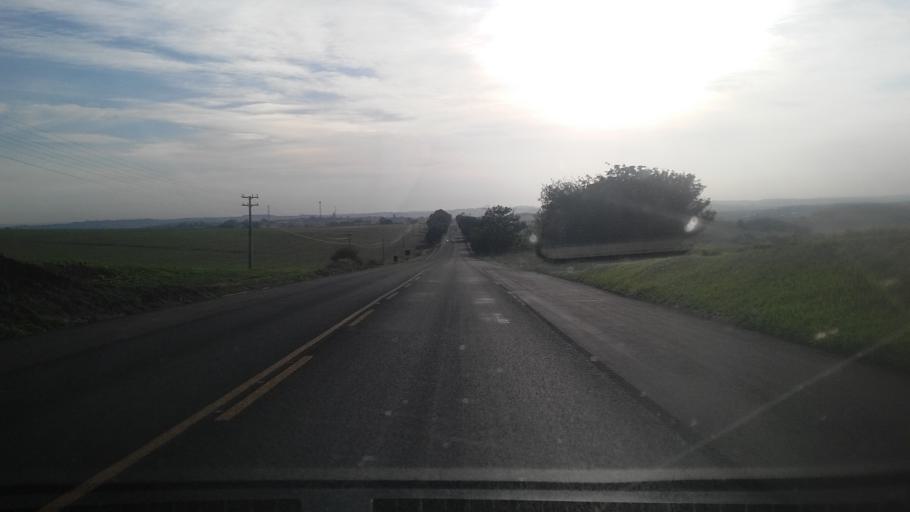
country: BR
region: Parana
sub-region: Bandeirantes
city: Bandeirantes
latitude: -23.1481
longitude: -50.5461
